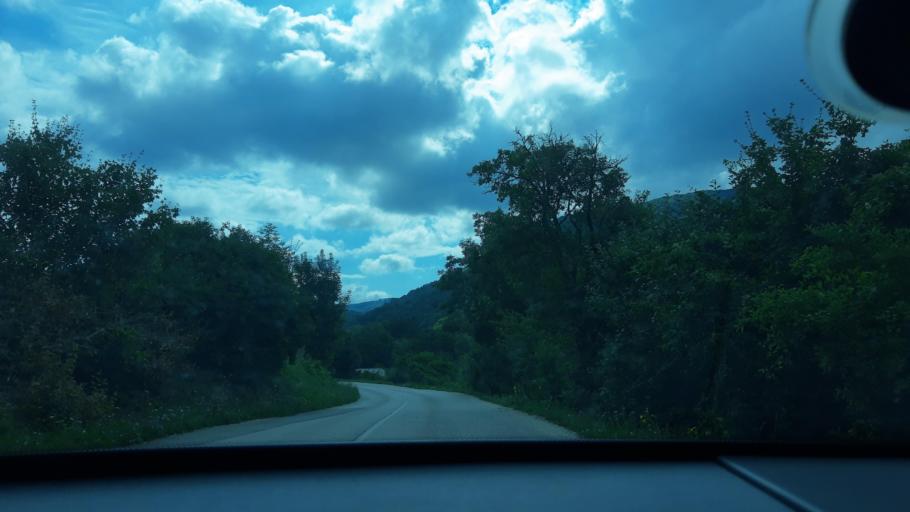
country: SK
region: Trnavsky
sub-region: Okres Trnava
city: Piestany
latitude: 48.6367
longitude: 17.9050
